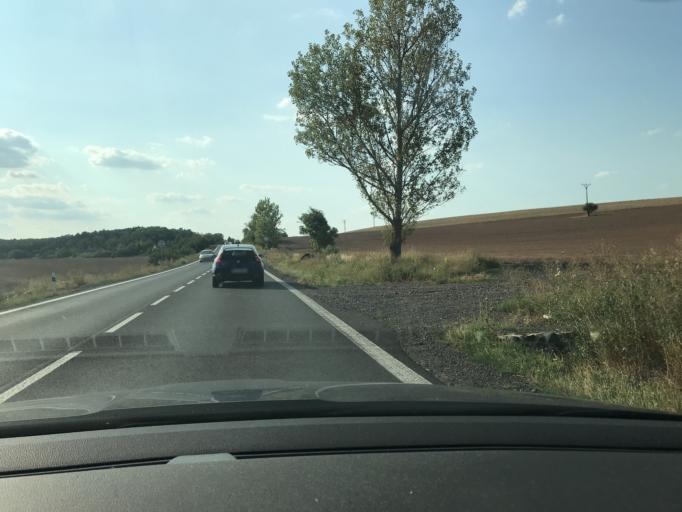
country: CZ
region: Central Bohemia
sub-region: Okres Kladno
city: Slany
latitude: 50.2509
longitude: 14.0349
